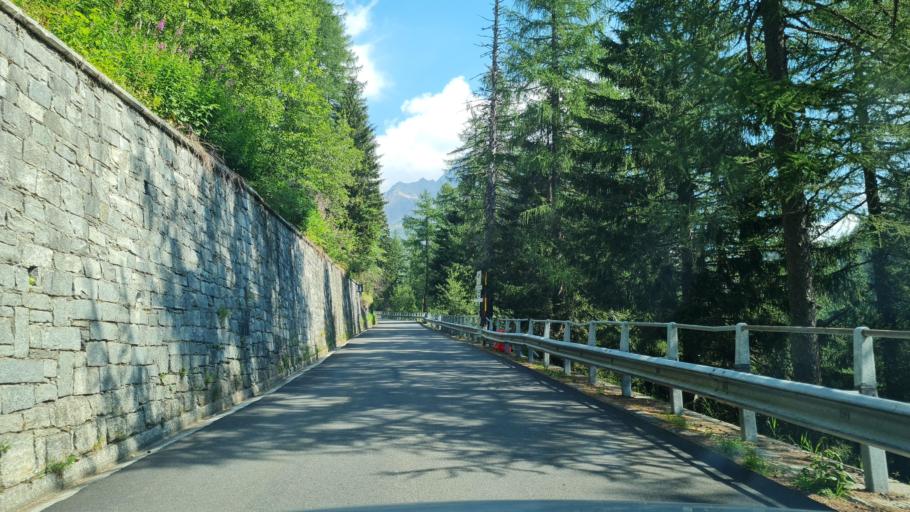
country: IT
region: Piedmont
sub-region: Provincia Verbano-Cusio-Ossola
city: Baceno
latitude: 46.3105
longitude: 8.2614
